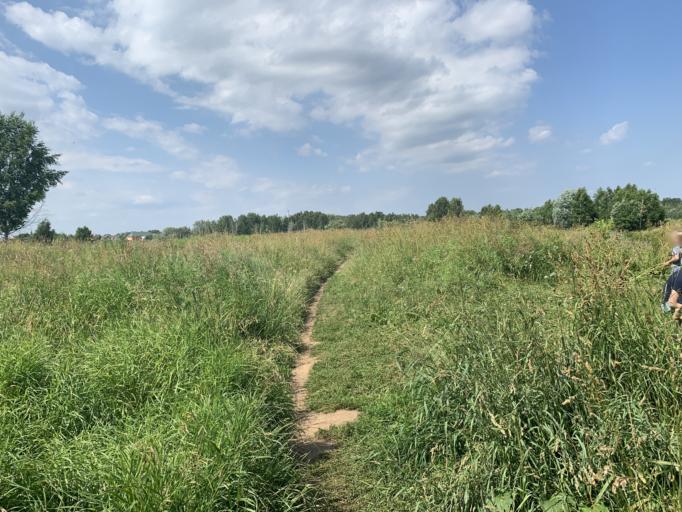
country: RU
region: Moskovskaya
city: Cherkizovo
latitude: 55.9746
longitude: 37.8004
